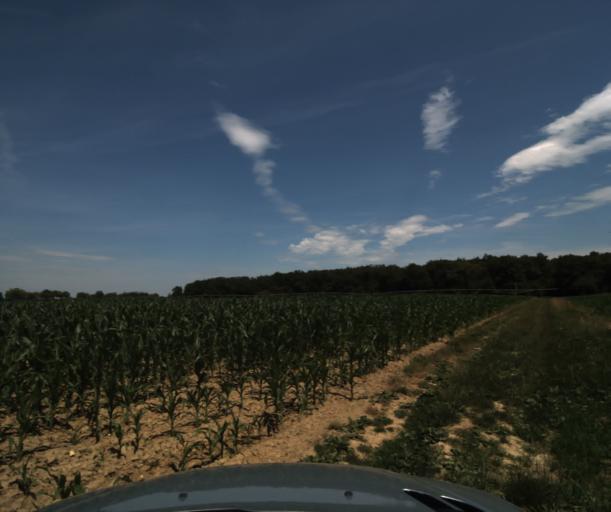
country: FR
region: Midi-Pyrenees
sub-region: Departement de la Haute-Garonne
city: Labastidette
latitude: 43.4641
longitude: 1.2247
